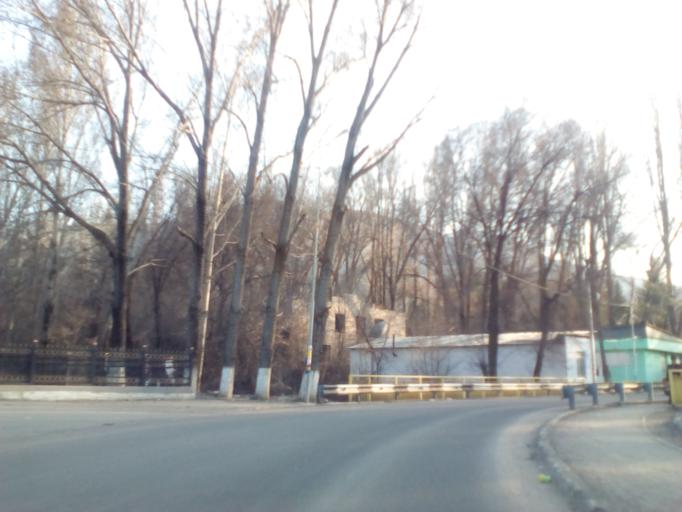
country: KZ
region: Almaty Oblysy
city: Burunday
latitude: 43.1575
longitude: 76.4181
